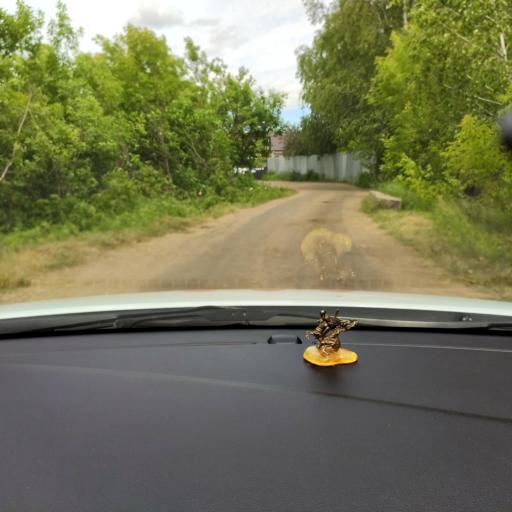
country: RU
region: Tatarstan
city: Staroye Arakchino
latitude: 55.8890
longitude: 49.0434
